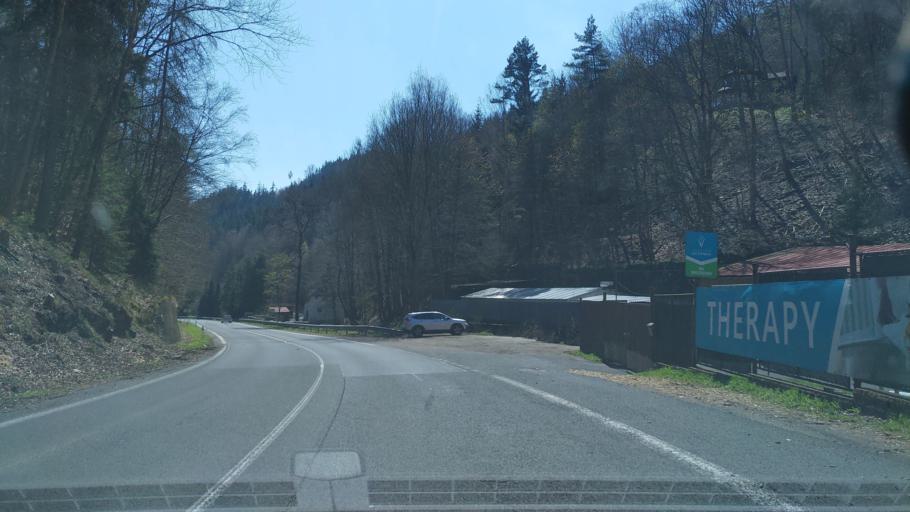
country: CZ
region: Karlovarsky
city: Jachymov
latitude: 50.3567
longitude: 12.9337
